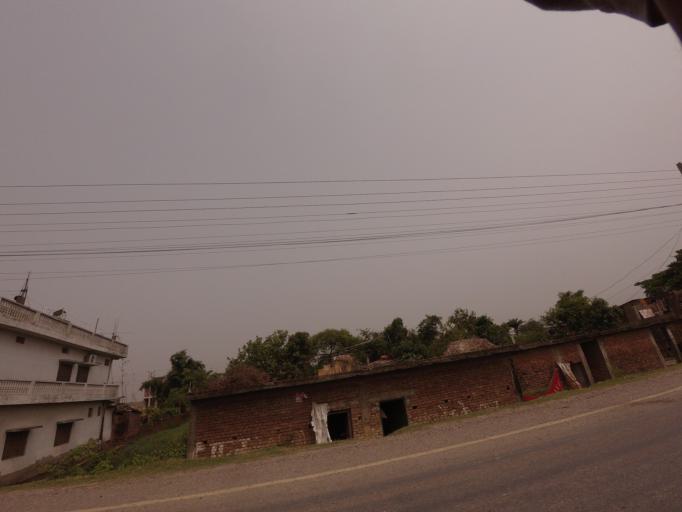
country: NP
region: Western Region
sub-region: Lumbini Zone
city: Bhairahawa
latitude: 27.5123
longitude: 83.3903
